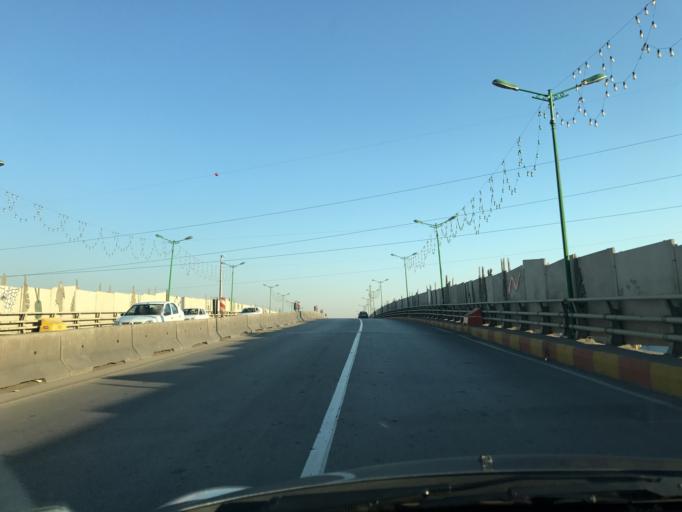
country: IR
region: Qazvin
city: Qazvin
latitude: 36.2891
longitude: 50.0054
